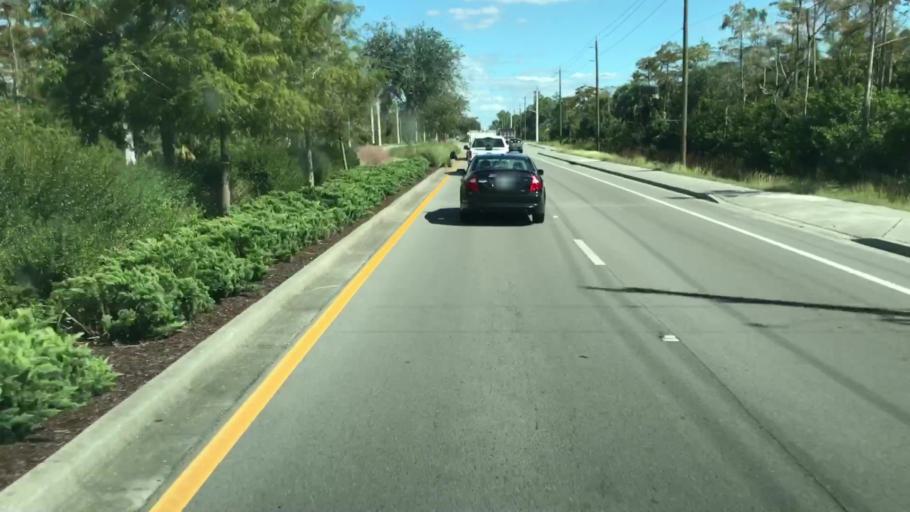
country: US
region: Florida
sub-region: Collier County
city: Orangetree
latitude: 26.2296
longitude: -81.6228
